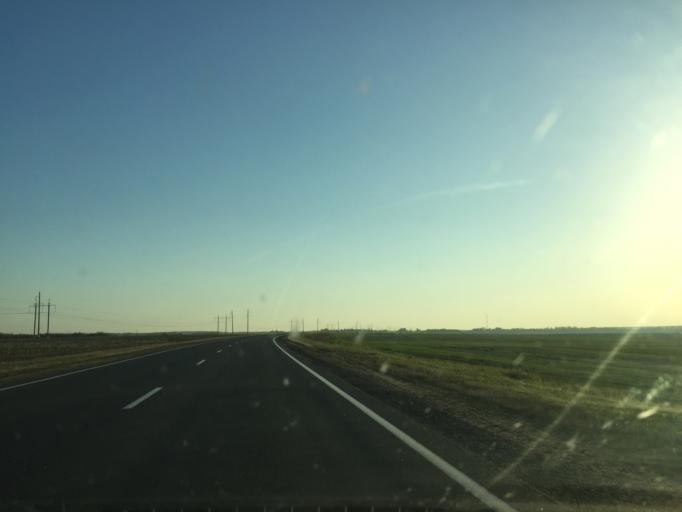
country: BY
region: Mogilev
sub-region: Mahilyowski Rayon
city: Kadino
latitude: 53.8319
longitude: 30.4780
